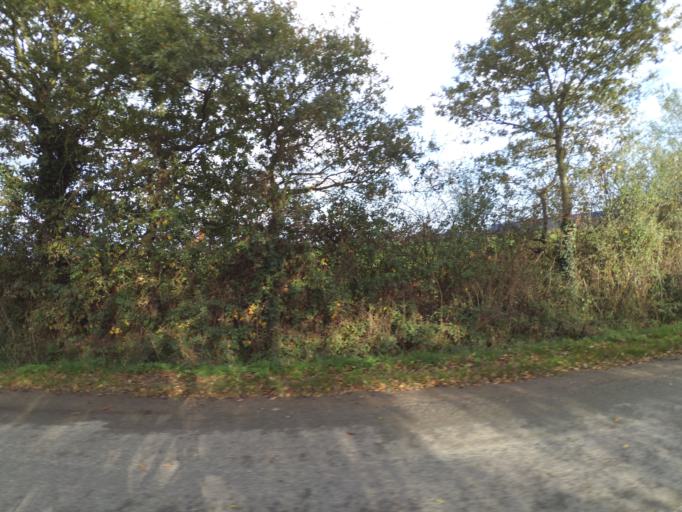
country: FR
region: Pays de la Loire
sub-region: Departement de la Vendee
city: Saint-Hilaire-de-Loulay
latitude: 47.0215
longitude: -1.3570
